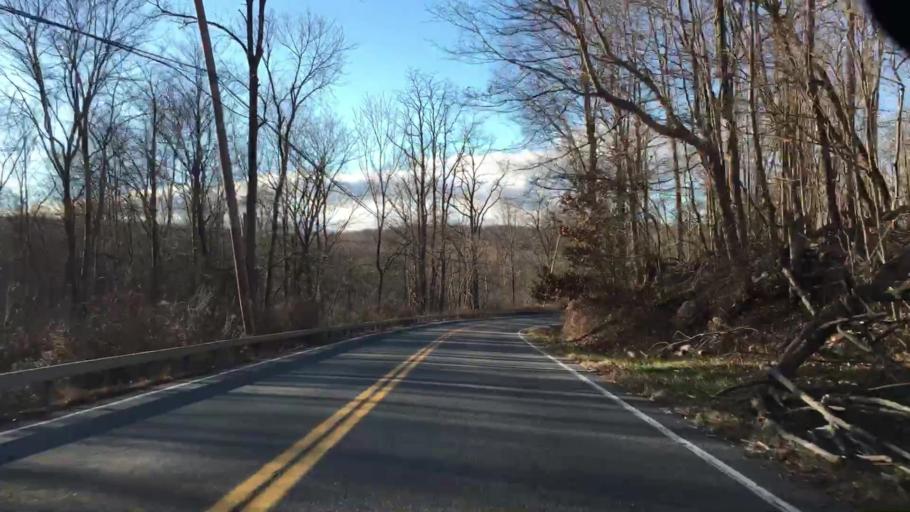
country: US
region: New York
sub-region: Putnam County
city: Lake Carmel
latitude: 41.4900
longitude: -73.6599
